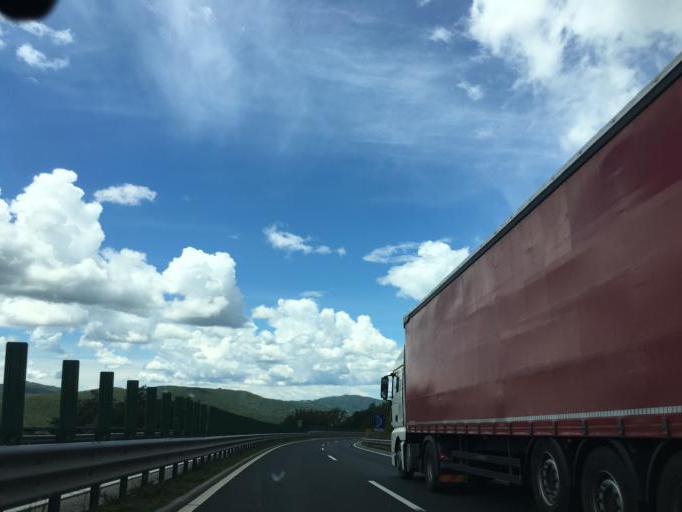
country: SI
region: Divaca
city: Divaca
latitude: 45.7646
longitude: 14.0366
